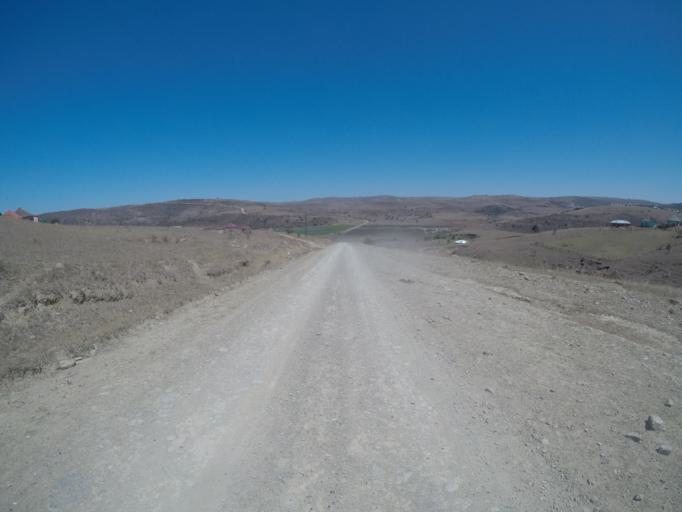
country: ZA
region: Eastern Cape
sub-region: OR Tambo District Municipality
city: Mthatha
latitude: -31.8645
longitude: 28.8726
